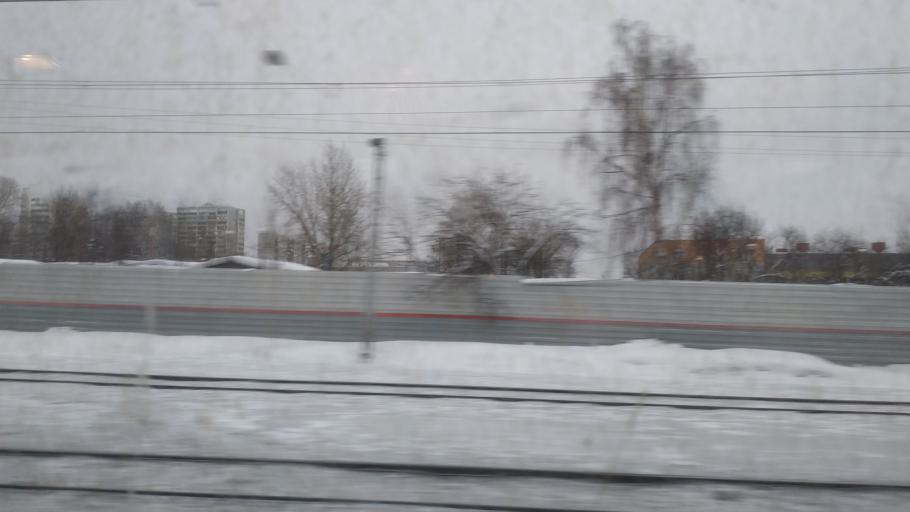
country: RU
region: Moskovskaya
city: Shcherbinka
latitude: 55.5366
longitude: 37.5697
